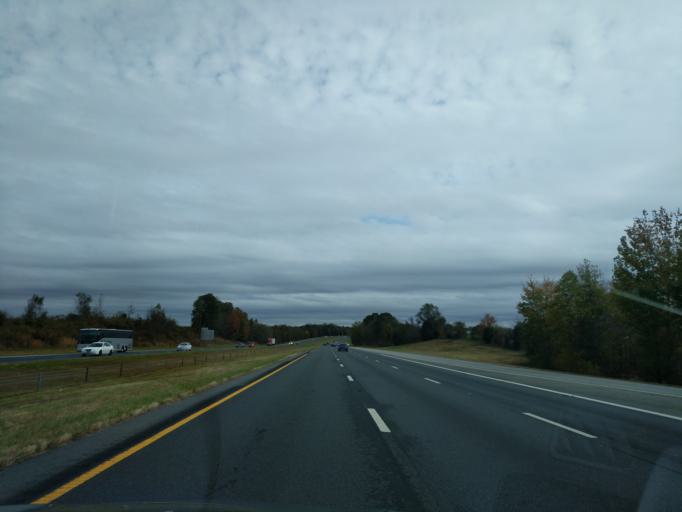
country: US
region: North Carolina
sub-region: Davidson County
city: Tyro
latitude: 35.7745
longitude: -80.3118
